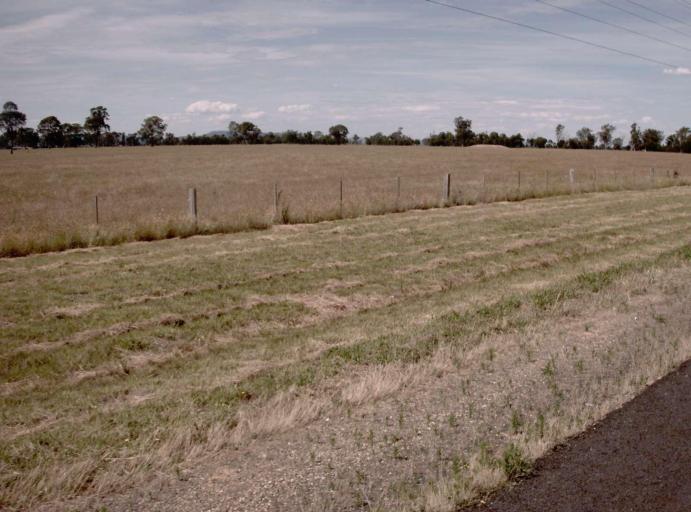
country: AU
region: Victoria
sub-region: East Gippsland
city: Bairnsdale
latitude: -37.8735
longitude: 147.4564
